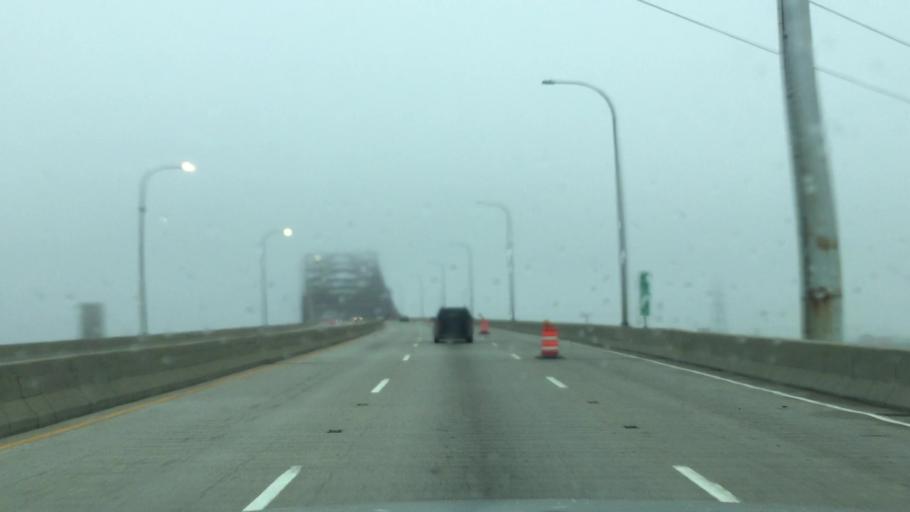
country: US
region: Indiana
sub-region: Lake County
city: Whiting
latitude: 41.7204
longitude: -87.5467
